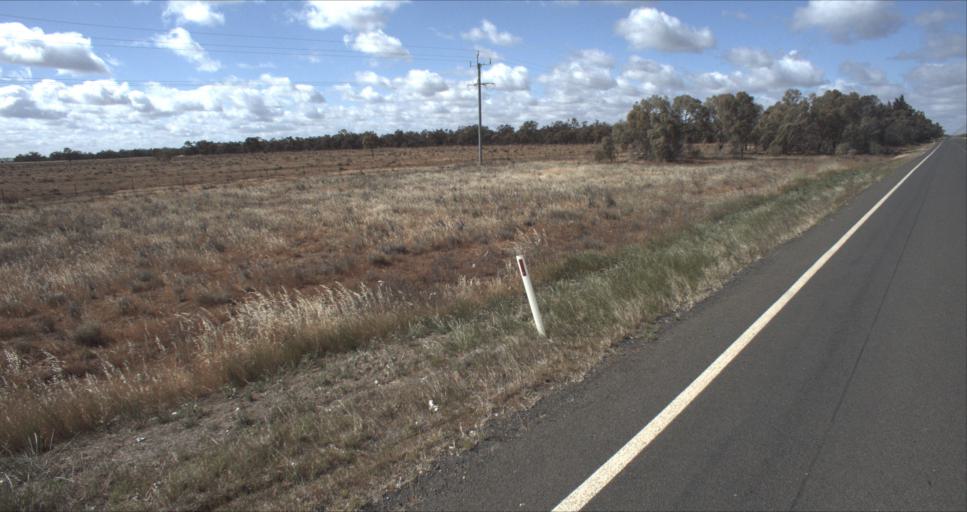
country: AU
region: New South Wales
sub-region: Murrumbidgee Shire
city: Darlington Point
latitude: -34.5259
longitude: 146.1749
